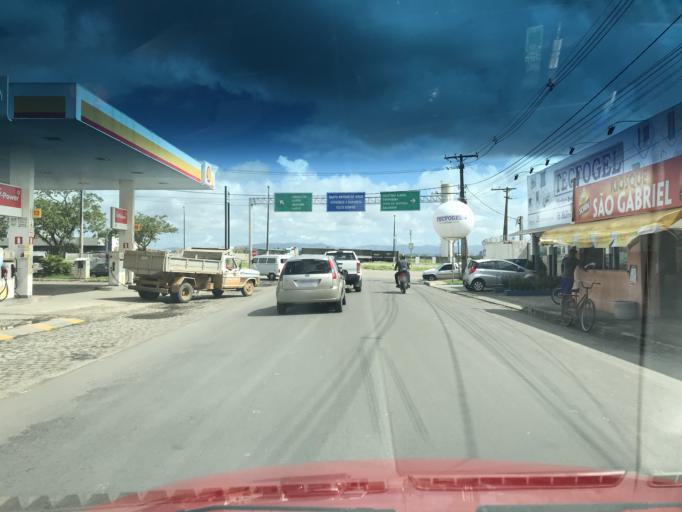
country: BR
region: Bahia
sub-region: Santo Antonio De Jesus
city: Santo Antonio de Jesus
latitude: -12.9646
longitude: -39.2713
